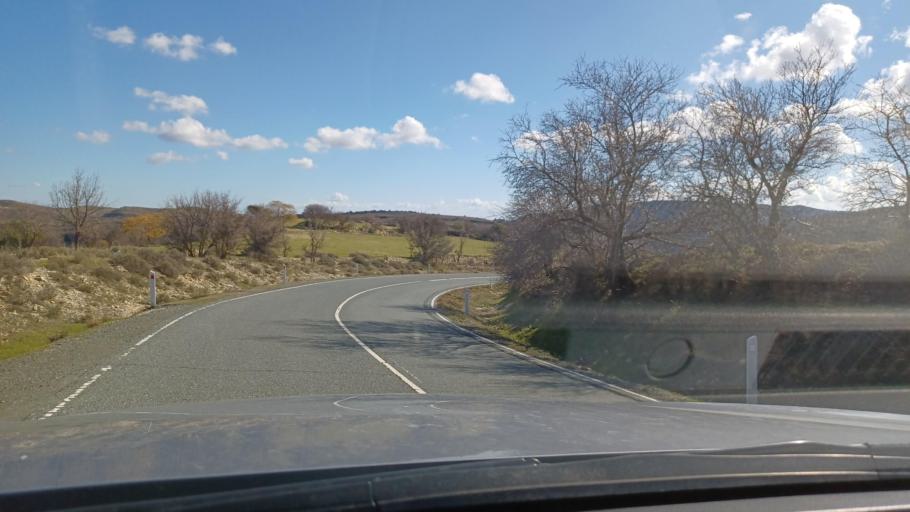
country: CY
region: Limassol
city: Pachna
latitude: 34.8183
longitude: 32.7744
